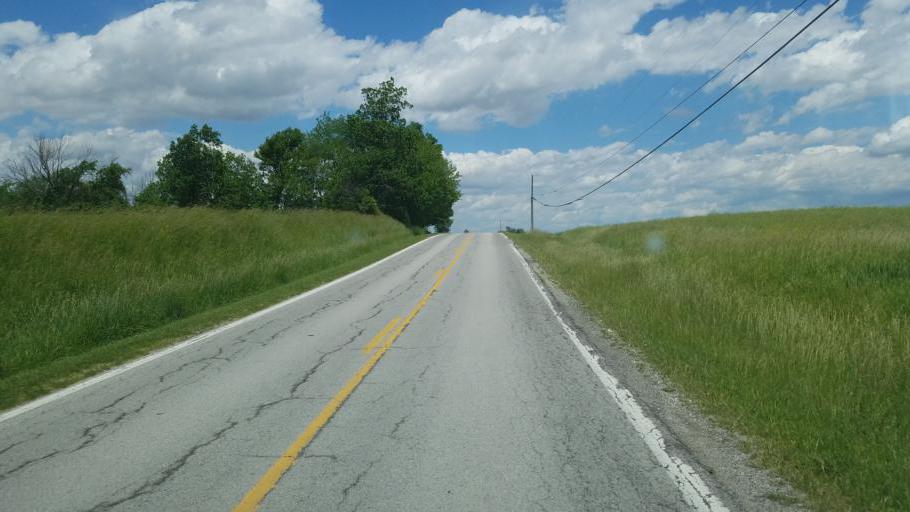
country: US
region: Ohio
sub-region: Huron County
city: Willard
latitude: 41.0875
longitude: -82.6847
